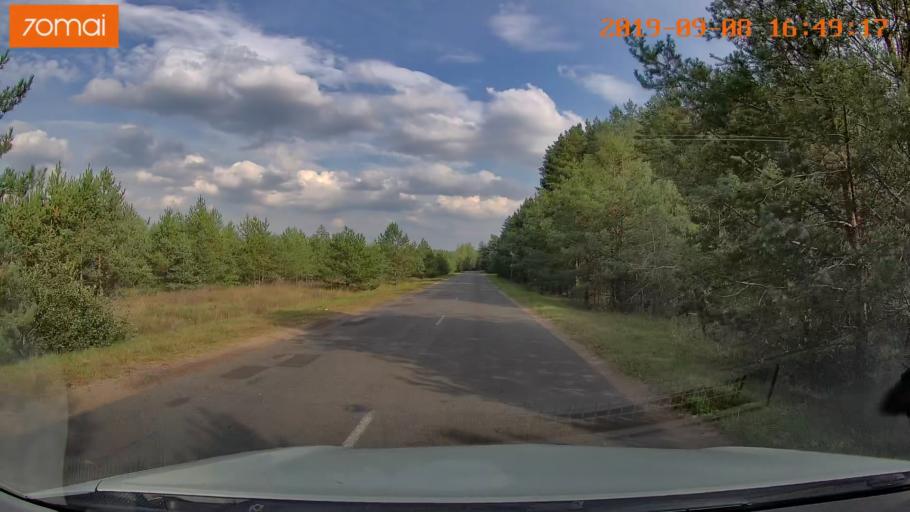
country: BY
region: Grodnenskaya
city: Hrodna
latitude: 53.8104
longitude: 23.8708
